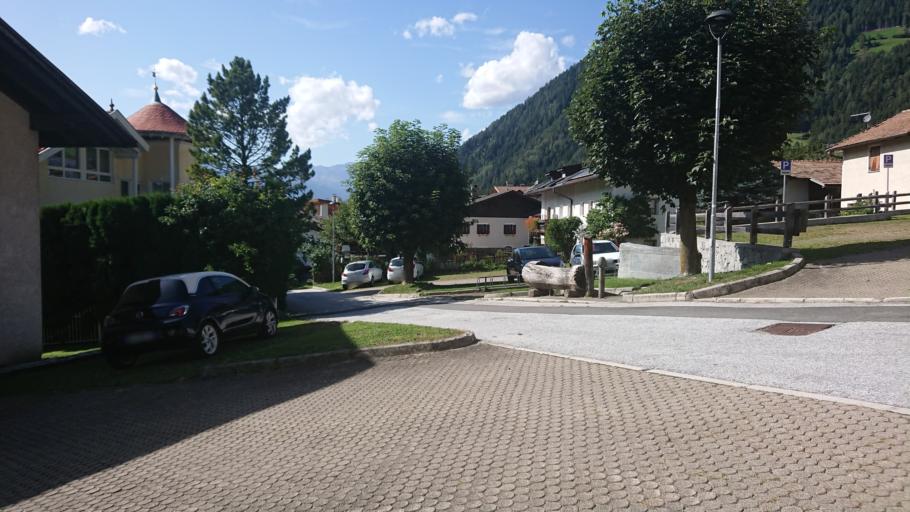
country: IT
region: Trentino-Alto Adige
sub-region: Bolzano
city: Campo di Trens
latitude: 46.8742
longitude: 11.4867
